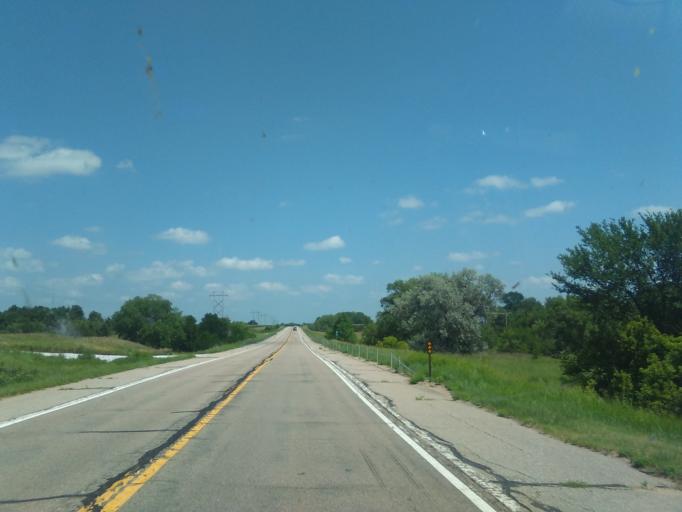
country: US
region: Nebraska
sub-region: Gosper County
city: Elwood
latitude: 40.6846
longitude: -99.8128
